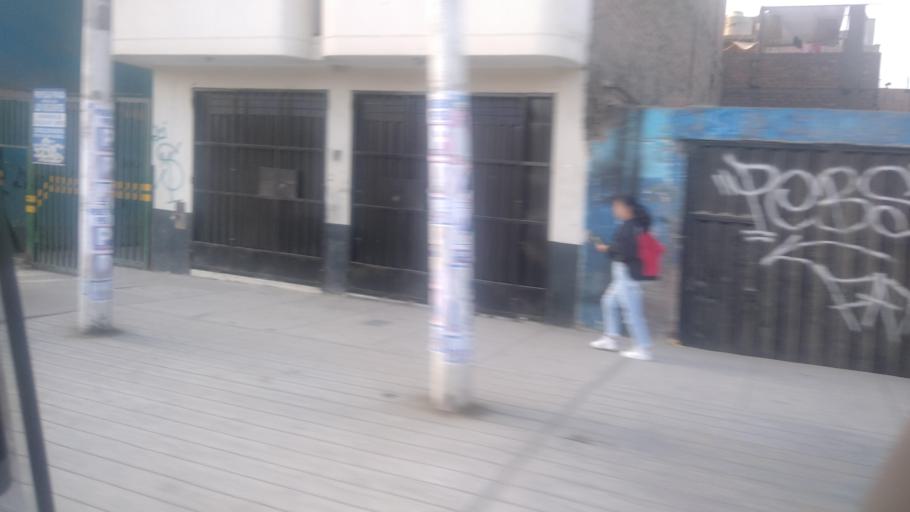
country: PE
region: Lima
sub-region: Lima
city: Vitarte
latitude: -12.0208
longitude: -76.9593
